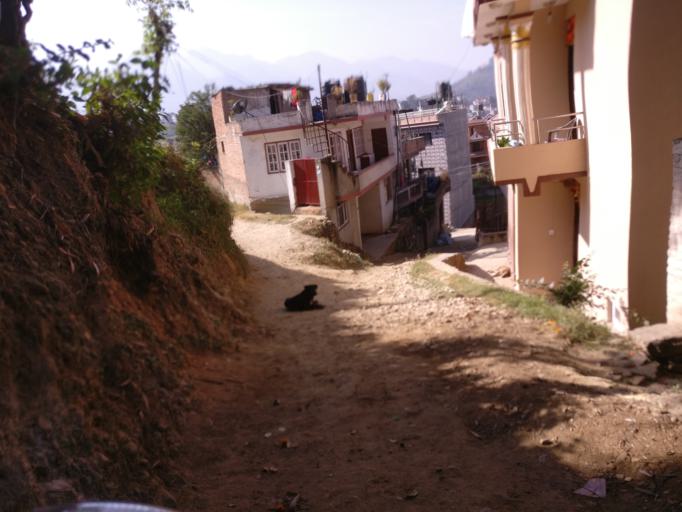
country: NP
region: Central Region
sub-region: Bagmati Zone
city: Patan
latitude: 27.6559
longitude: 85.3144
